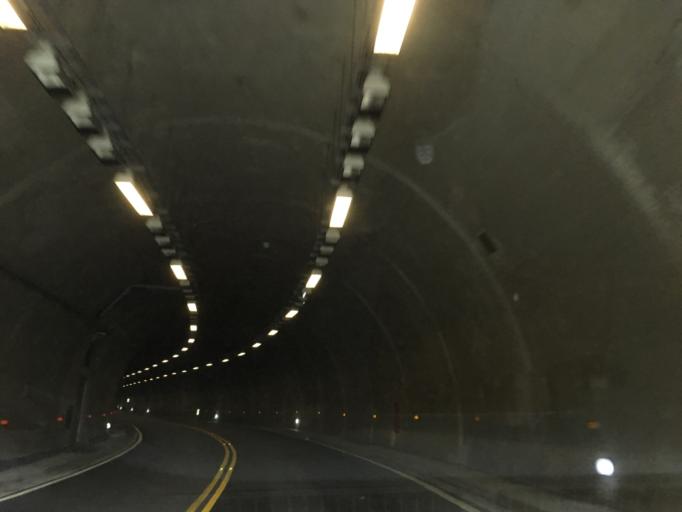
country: TW
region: Taiwan
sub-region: Hualien
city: Hualian
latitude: 24.1730
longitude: 121.5719
